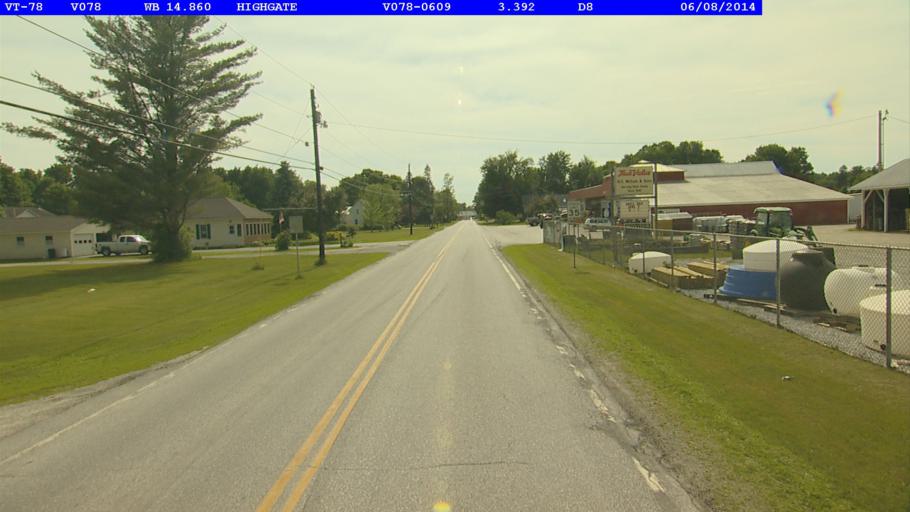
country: US
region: Vermont
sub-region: Franklin County
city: Swanton
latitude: 44.9401
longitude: -73.0391
